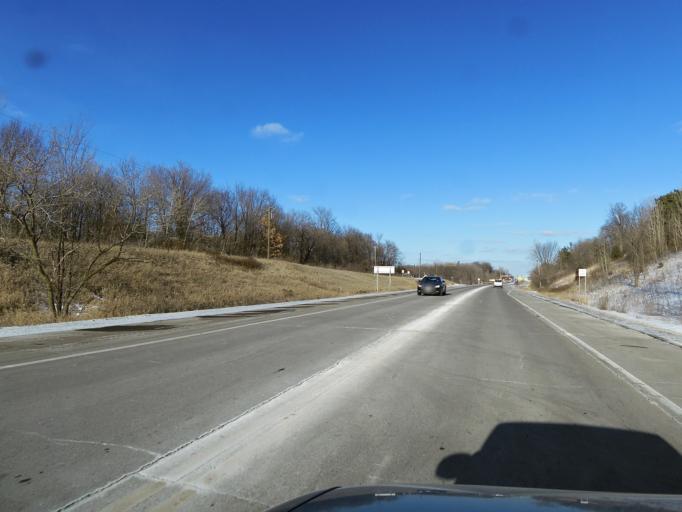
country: US
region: Minnesota
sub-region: Scott County
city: Prior Lake
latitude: 44.7230
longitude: -93.4096
